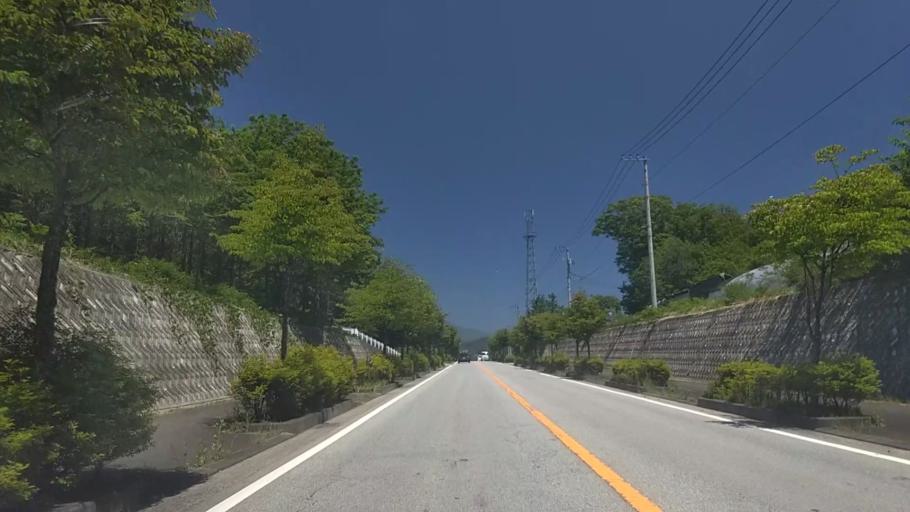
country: JP
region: Yamanashi
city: Nirasaki
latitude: 35.8191
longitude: 138.4293
